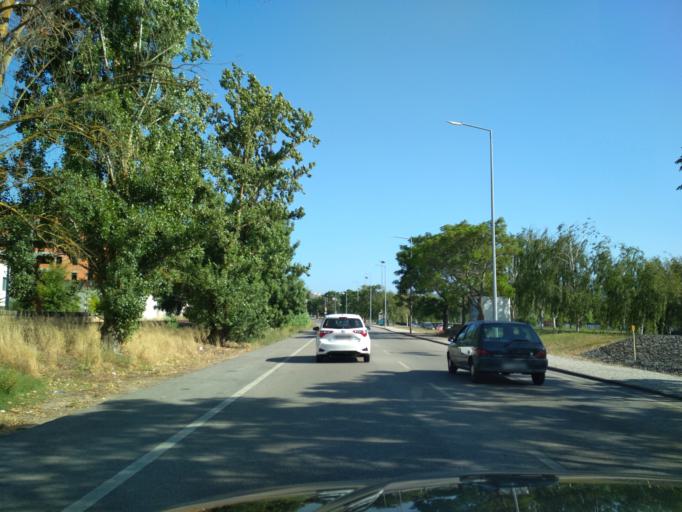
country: PT
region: Coimbra
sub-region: Coimbra
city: Coimbra
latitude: 40.2026
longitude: -8.4247
